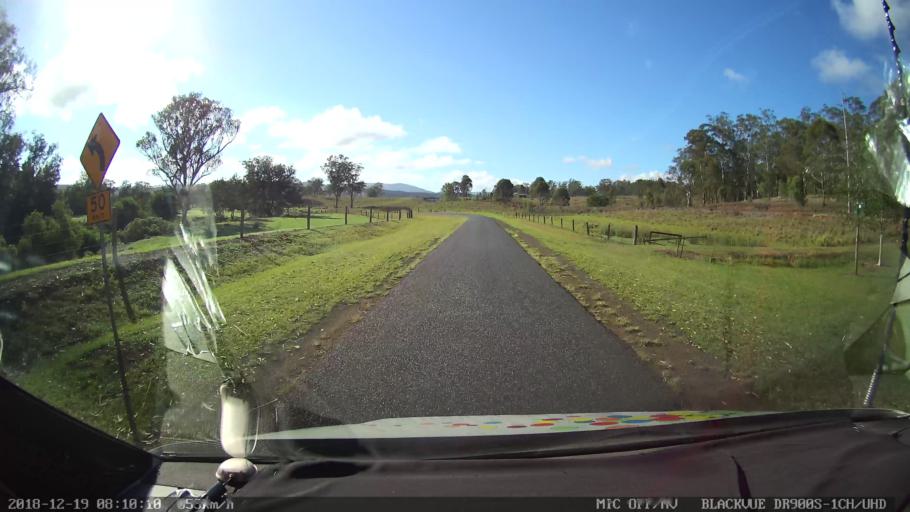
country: AU
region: Queensland
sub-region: Logan
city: Cedar Vale
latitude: -28.2146
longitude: 152.8836
